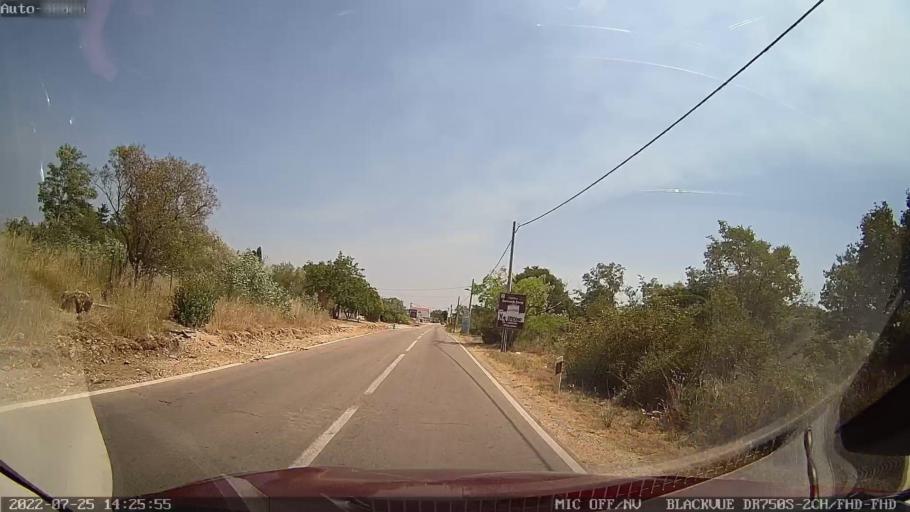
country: HR
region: Zadarska
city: Policnik
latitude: 44.1420
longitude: 15.3345
